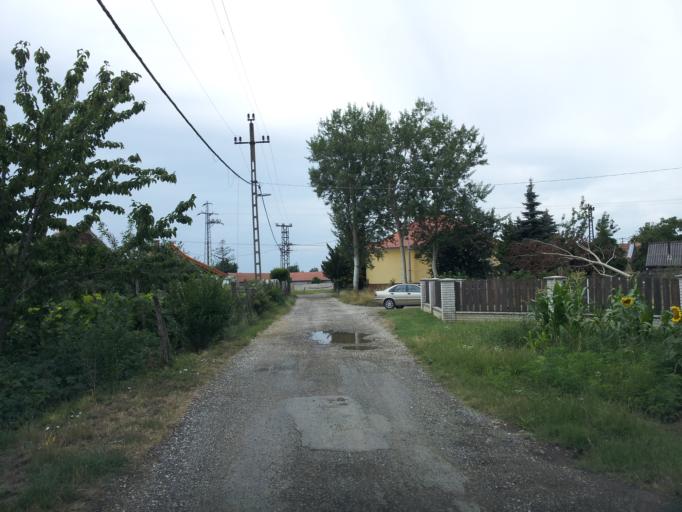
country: HU
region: Vas
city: Vasvar
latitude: 47.0522
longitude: 16.8122
